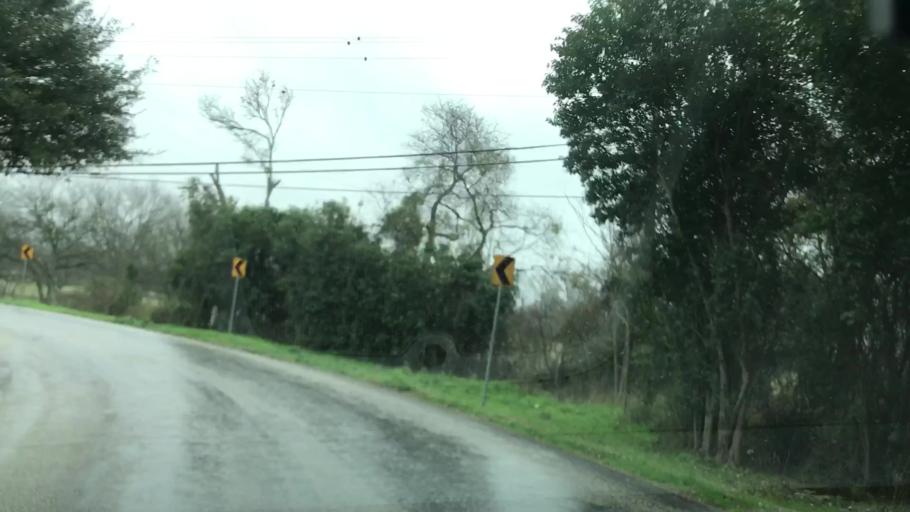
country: US
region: Texas
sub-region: Hays County
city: San Marcos
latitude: 29.8943
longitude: -97.8980
